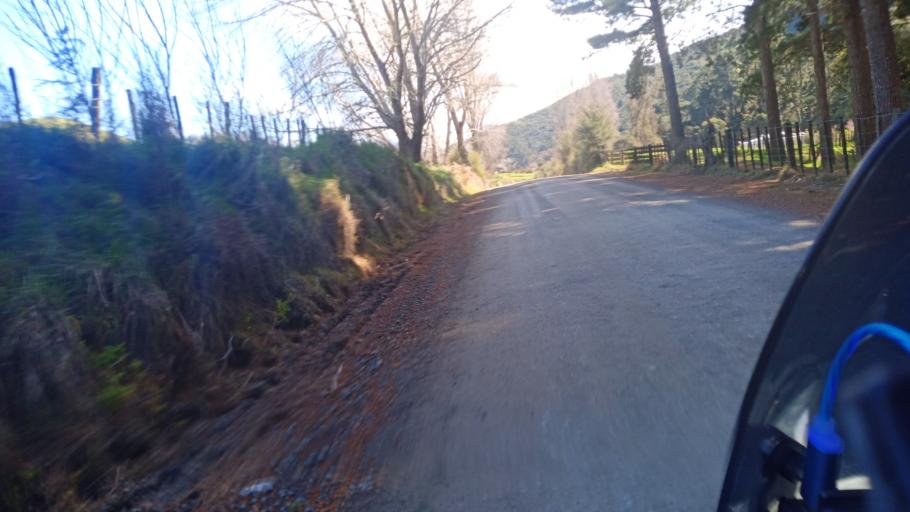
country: NZ
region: Gisborne
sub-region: Gisborne District
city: Gisborne
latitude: -37.9944
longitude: 178.3079
